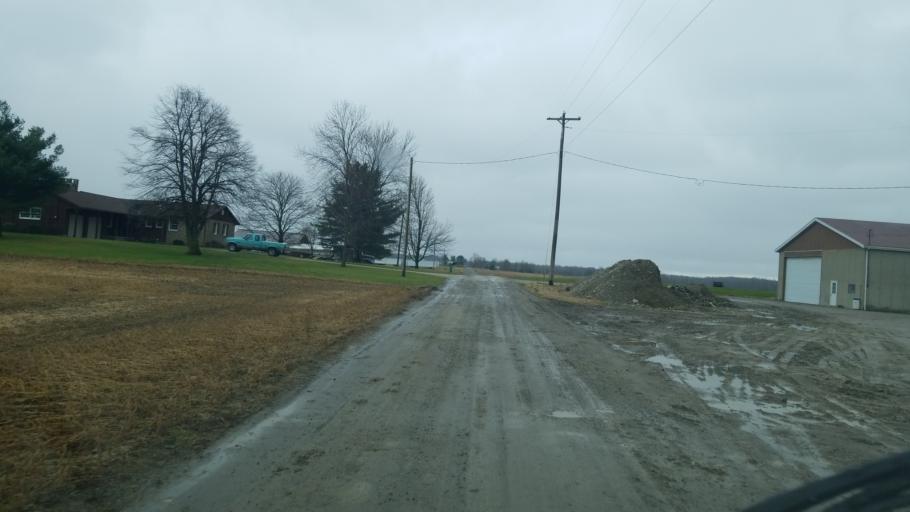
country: US
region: Ohio
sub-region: Ashtabula County
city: Roaming Shores
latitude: 41.5819
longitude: -80.7193
